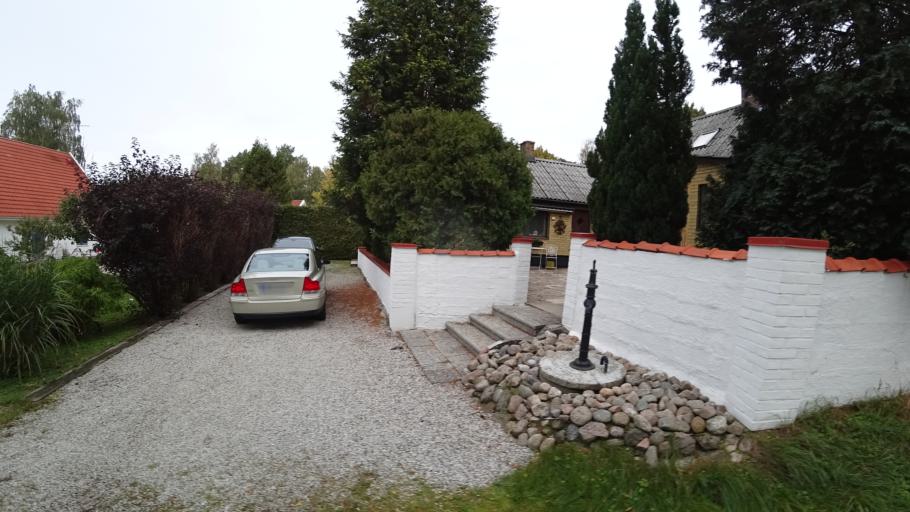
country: SE
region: Skane
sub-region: Kavlinge Kommun
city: Hofterup
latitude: 55.8089
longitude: 12.9724
